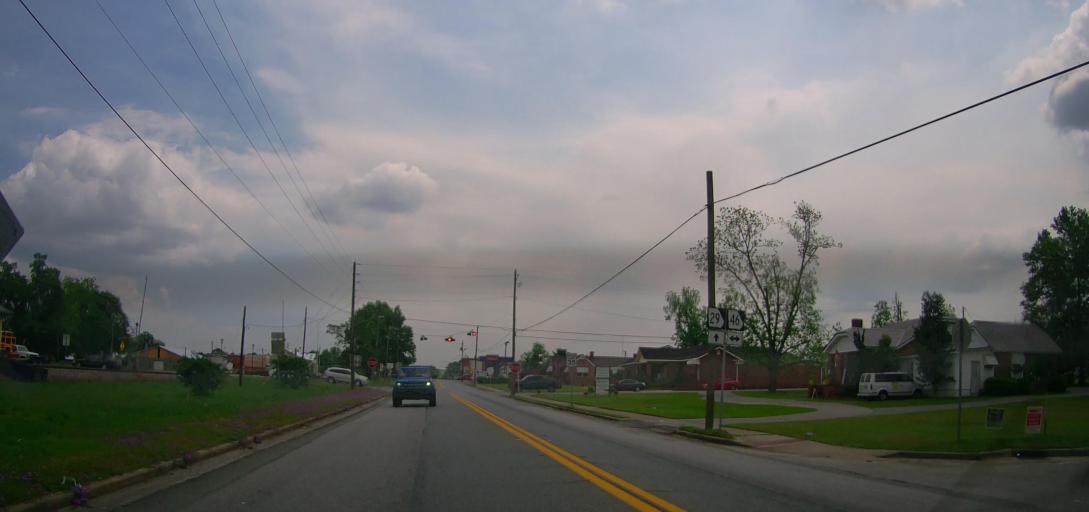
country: US
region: Georgia
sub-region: Treutlen County
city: Soperton
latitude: 32.3794
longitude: -82.5947
